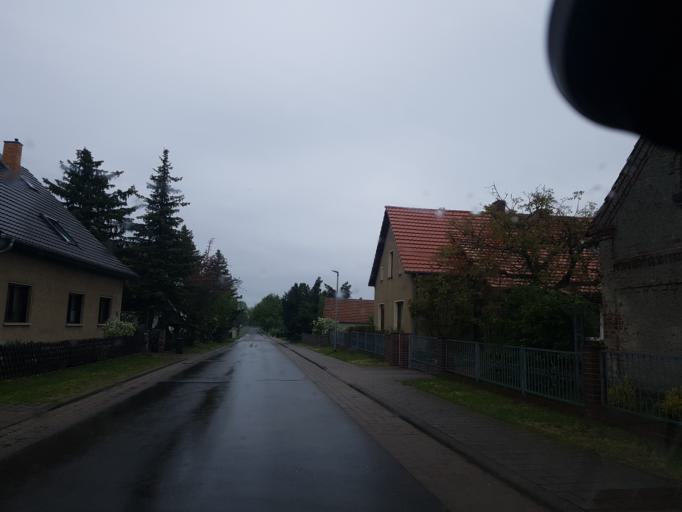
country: DE
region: Saxony
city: Gross Duben
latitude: 51.6713
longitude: 14.4718
